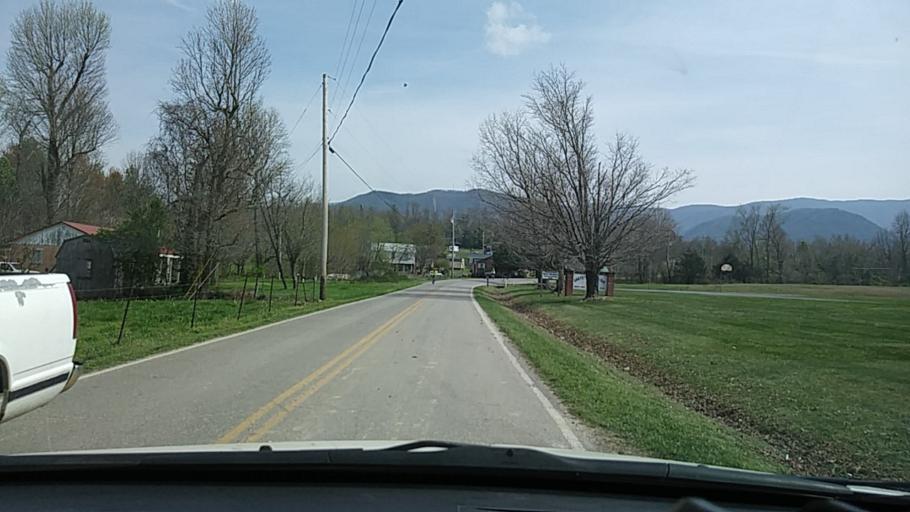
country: US
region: Tennessee
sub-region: Greene County
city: Tusculum
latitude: 36.0948
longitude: -82.7304
